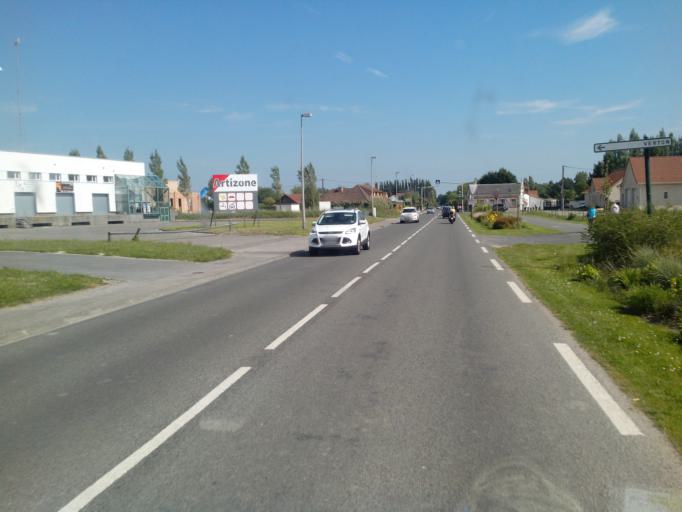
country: FR
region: Nord-Pas-de-Calais
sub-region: Departement du Pas-de-Calais
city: Groffliers
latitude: 50.3889
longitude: 1.6084
